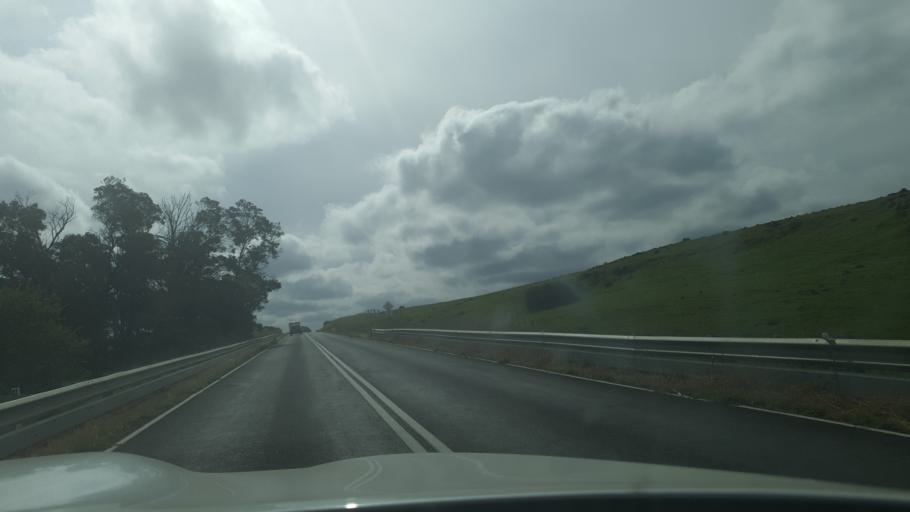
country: AU
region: Victoria
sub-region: Central Goldfields
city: Maryborough
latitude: -37.2130
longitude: 143.7259
